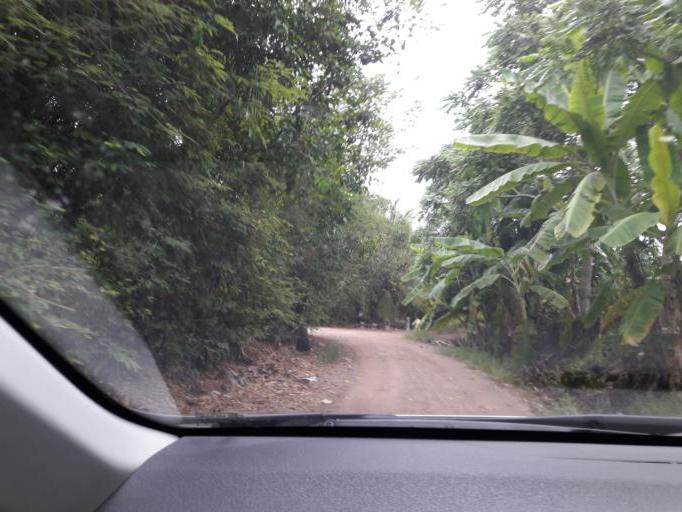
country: TH
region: Ratchaburi
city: Damnoen Saduak
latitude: 13.5441
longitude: 100.0089
